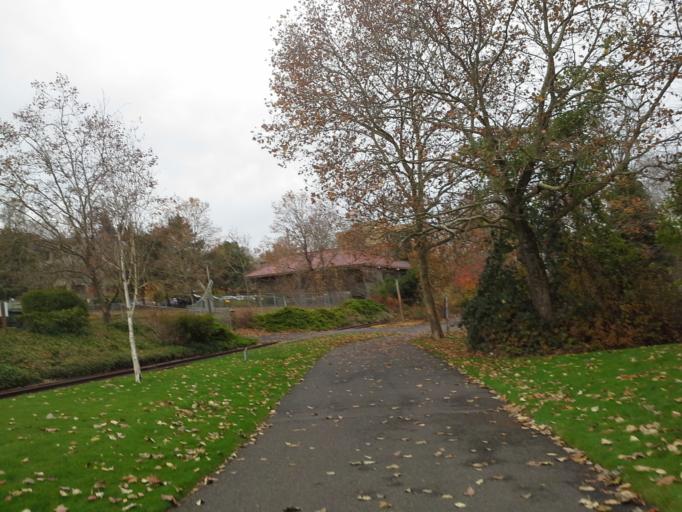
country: US
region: Oregon
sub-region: Multnomah County
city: Portland
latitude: 45.4874
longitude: -122.6729
